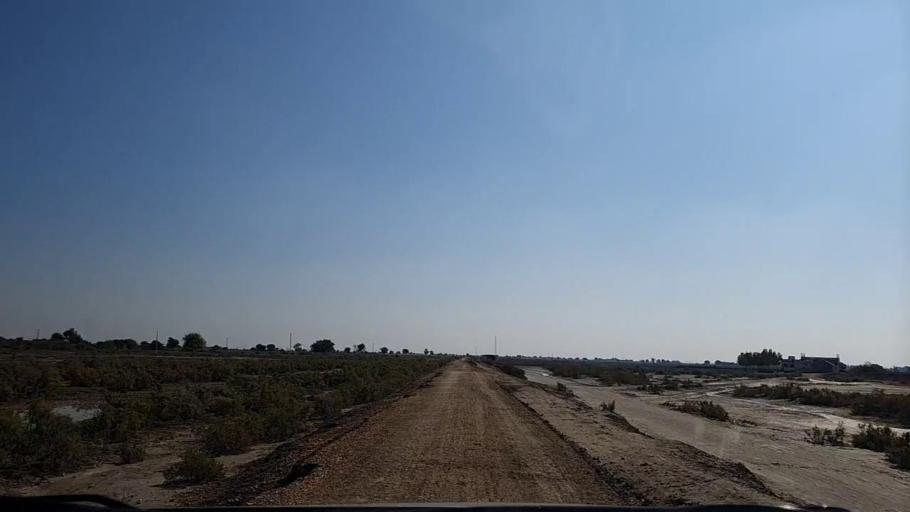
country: PK
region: Sindh
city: Pithoro
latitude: 25.7034
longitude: 69.3385
